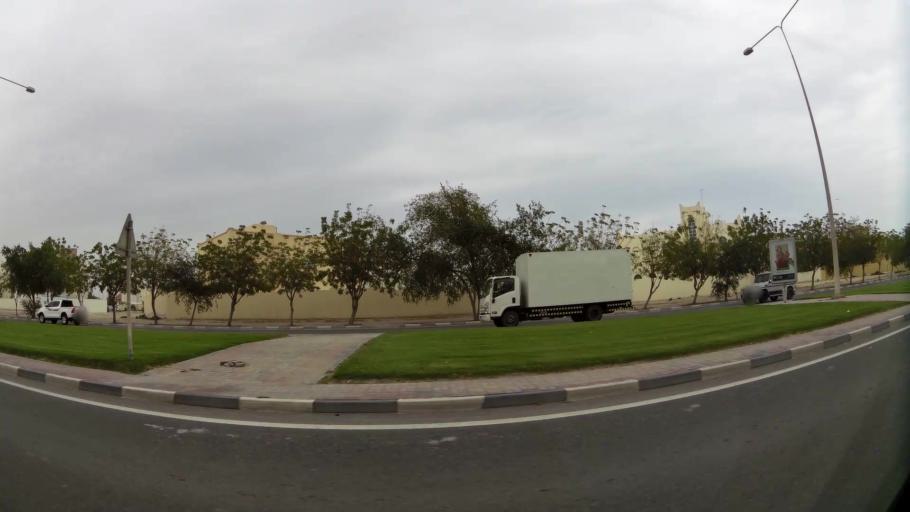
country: QA
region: Baladiyat ad Dawhah
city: Doha
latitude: 25.3481
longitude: 51.5035
